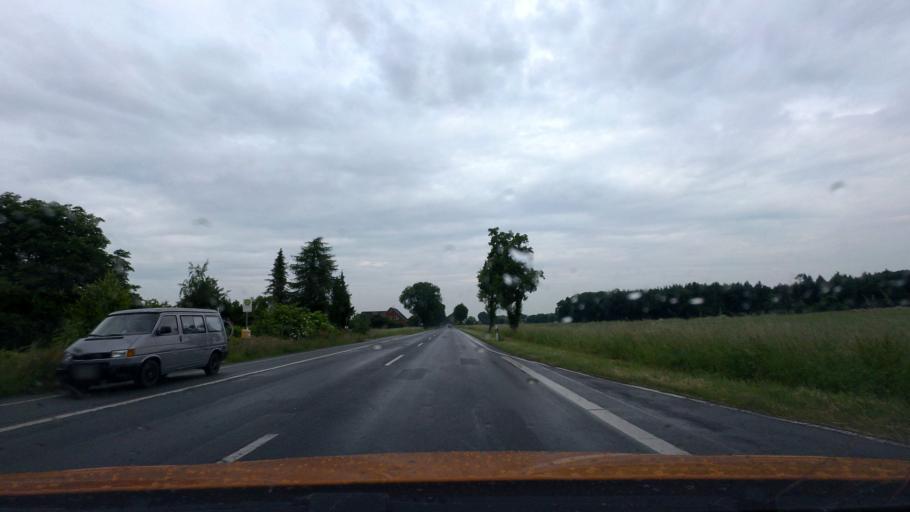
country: DE
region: Lower Saxony
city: Sustedt
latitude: 52.8438
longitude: 8.9007
